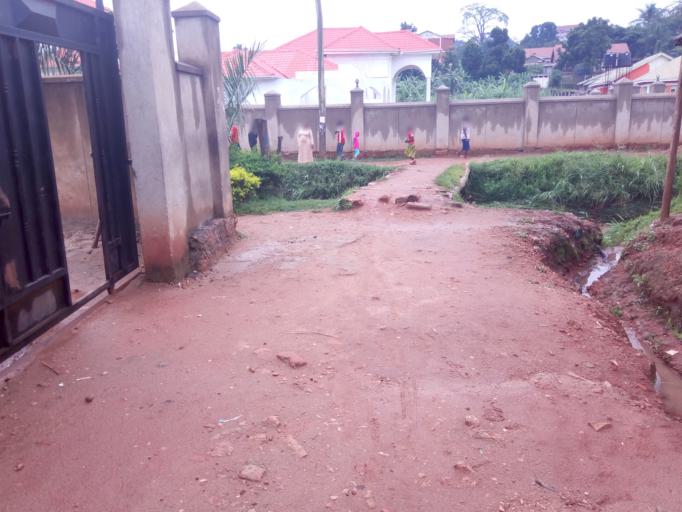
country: UG
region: Central Region
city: Kampala Central Division
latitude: 0.3414
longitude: 32.5581
